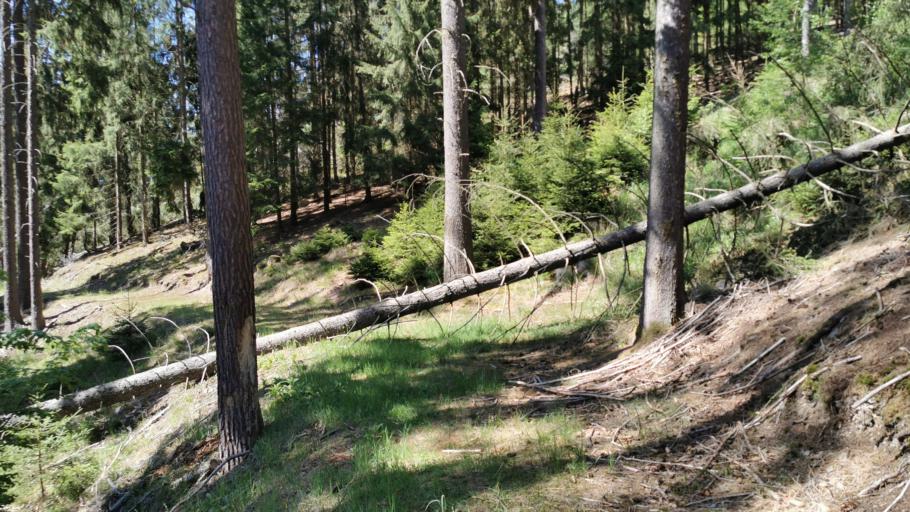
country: DE
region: Thuringia
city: Essbach
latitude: 50.5713
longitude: 11.6933
